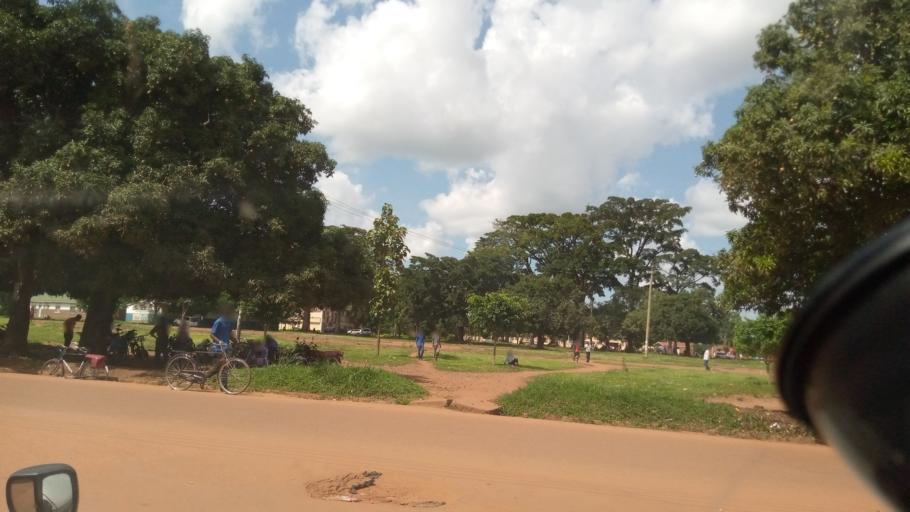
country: UG
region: Northern Region
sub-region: Lira District
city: Lira
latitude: 2.2472
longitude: 32.8986
